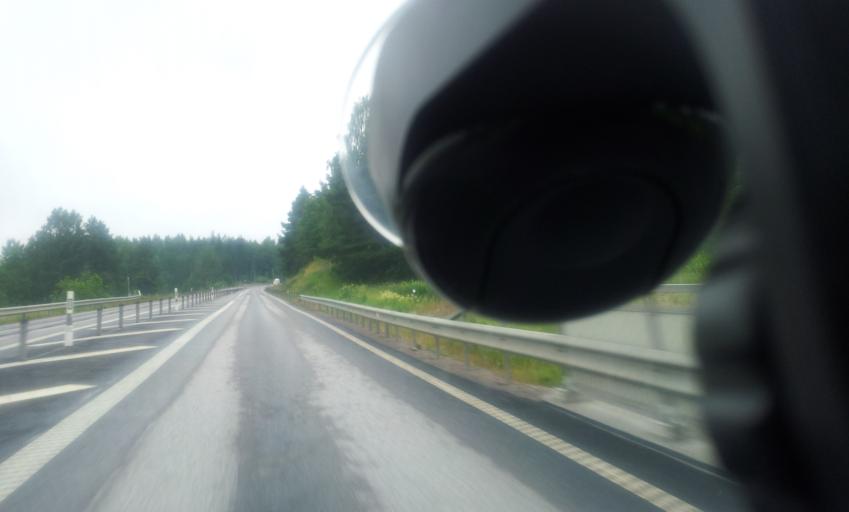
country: SE
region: Kalmar
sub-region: Vasterviks Kommun
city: Gamleby
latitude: 57.9198
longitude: 16.3996
